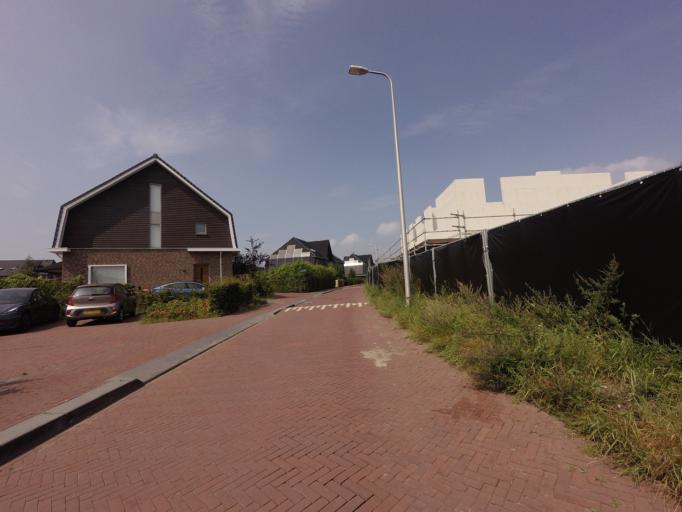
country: NL
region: North Holland
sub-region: Gemeente Huizen
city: Huizen
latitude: 52.2900
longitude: 5.2791
